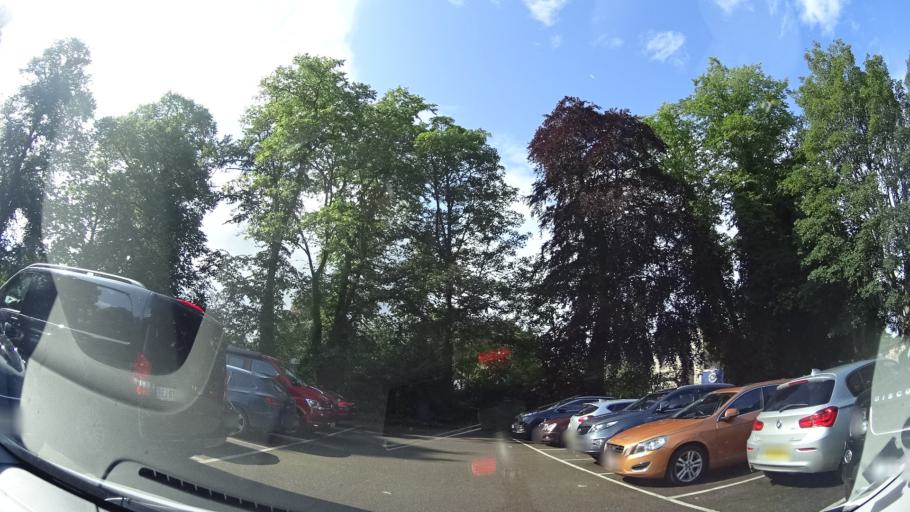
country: GB
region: Scotland
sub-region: Highland
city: Inverness
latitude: 57.4739
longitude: -4.2295
